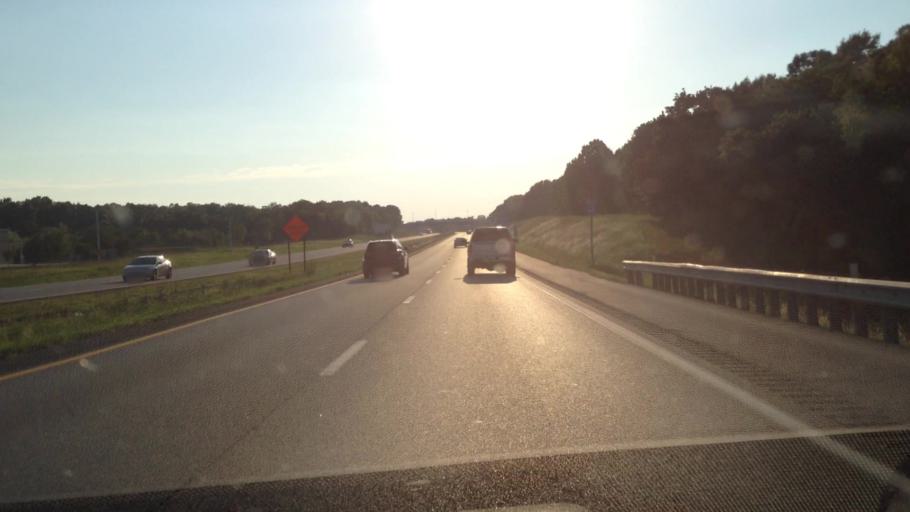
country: US
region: Missouri
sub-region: Jasper County
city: Duquesne
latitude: 37.0462
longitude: -94.4883
